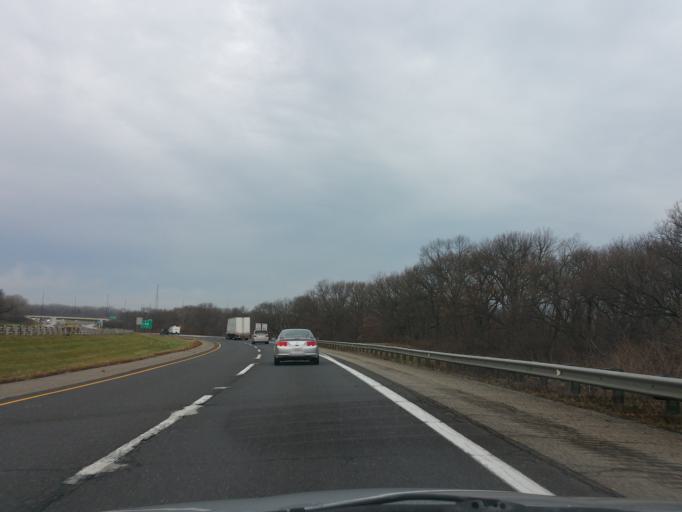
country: US
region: Indiana
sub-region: Porter County
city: Portage
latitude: 41.5854
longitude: -87.2038
